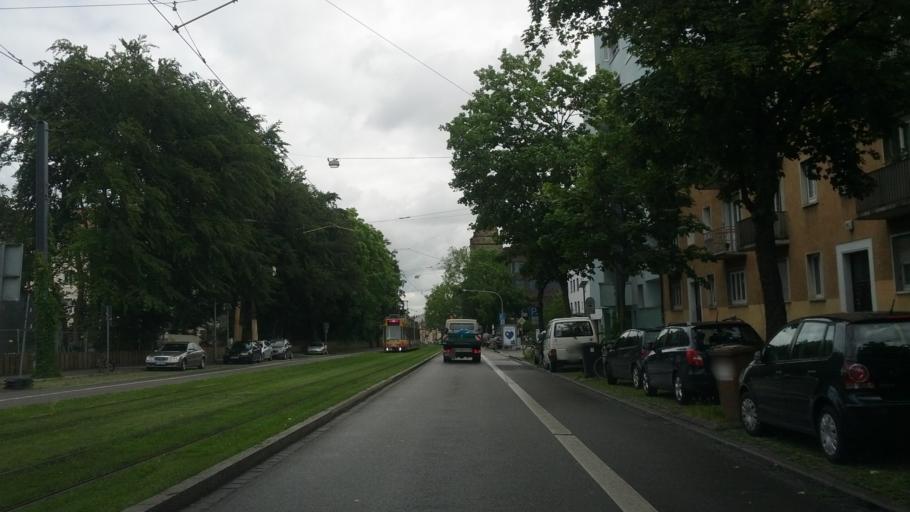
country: DE
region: Baden-Wuerttemberg
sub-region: Freiburg Region
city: Freiburg
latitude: 48.0003
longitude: 7.8539
